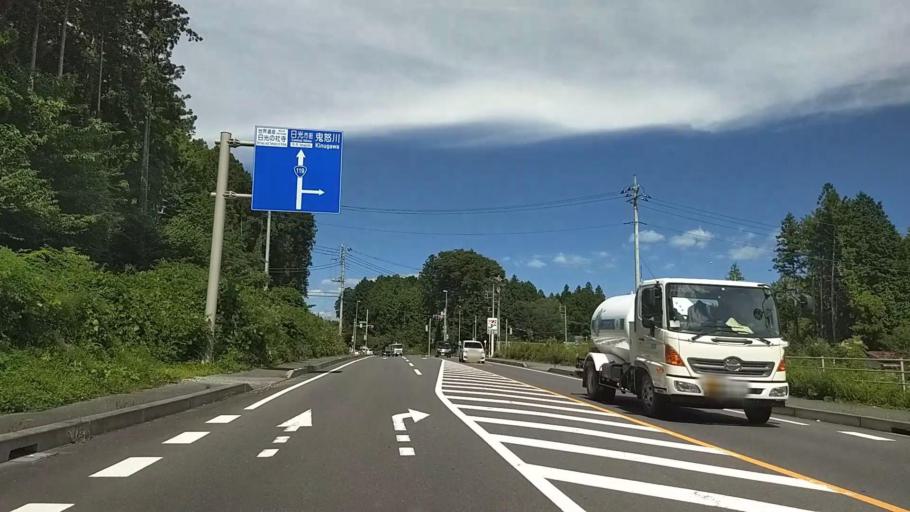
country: JP
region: Tochigi
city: Imaichi
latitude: 36.7002
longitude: 139.7534
